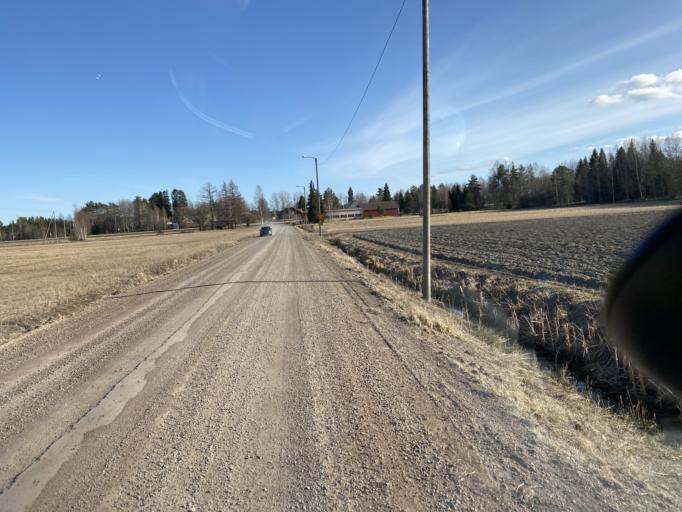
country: FI
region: Satakunta
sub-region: Rauma
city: Lappi
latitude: 61.1265
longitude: 21.9527
